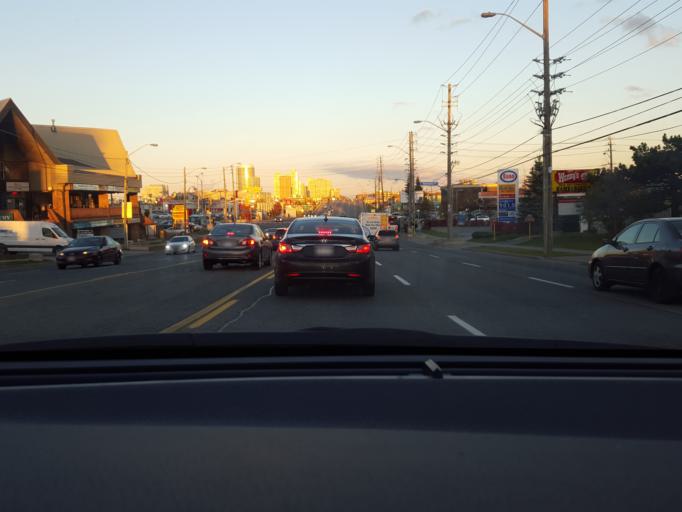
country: CA
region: Ontario
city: Scarborough
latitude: 43.7654
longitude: -79.2828
